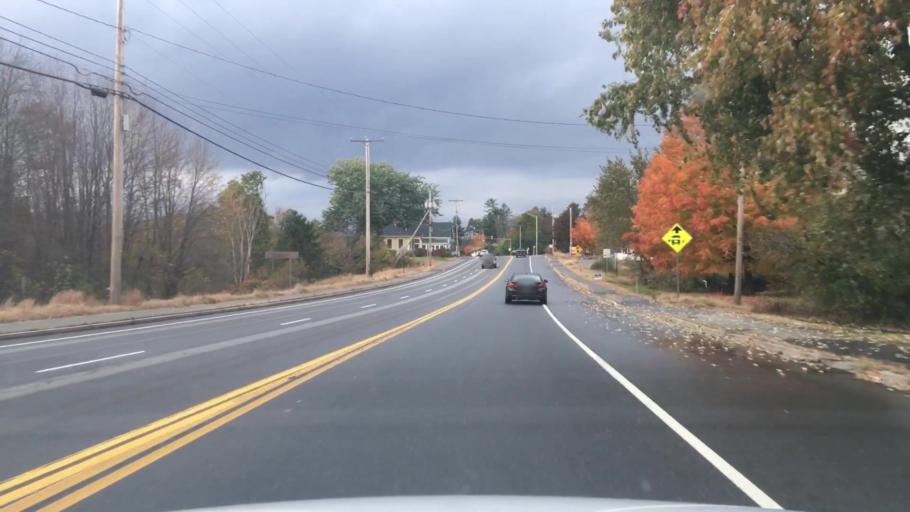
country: US
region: New Hampshire
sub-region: Merrimack County
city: Epsom
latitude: 43.2257
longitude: -71.3474
